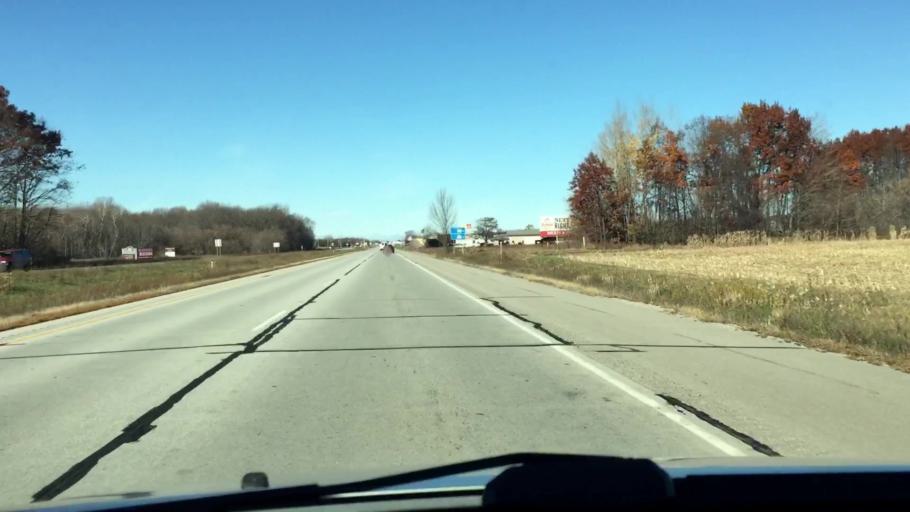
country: US
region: Wisconsin
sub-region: Brown County
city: Howard
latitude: 44.5703
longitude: -88.1551
